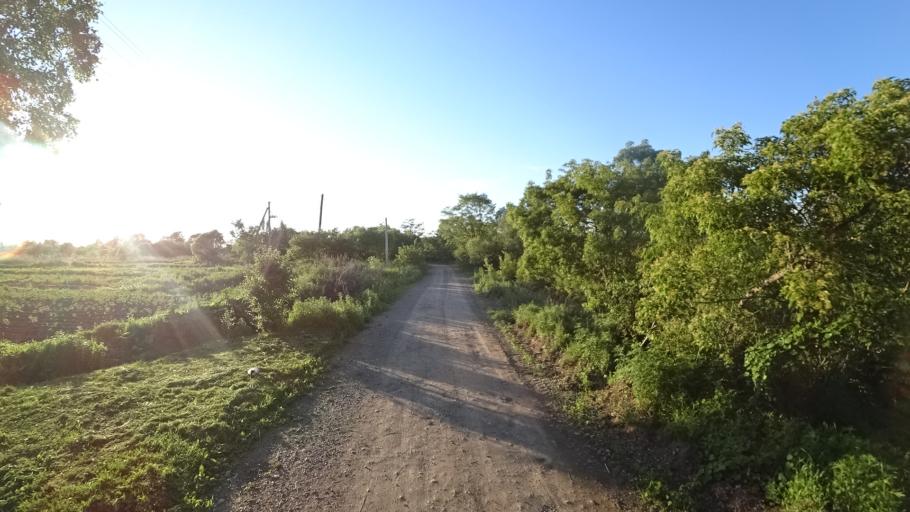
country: RU
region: Khabarovsk Krai
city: Khor
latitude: 47.8565
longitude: 135.0017
